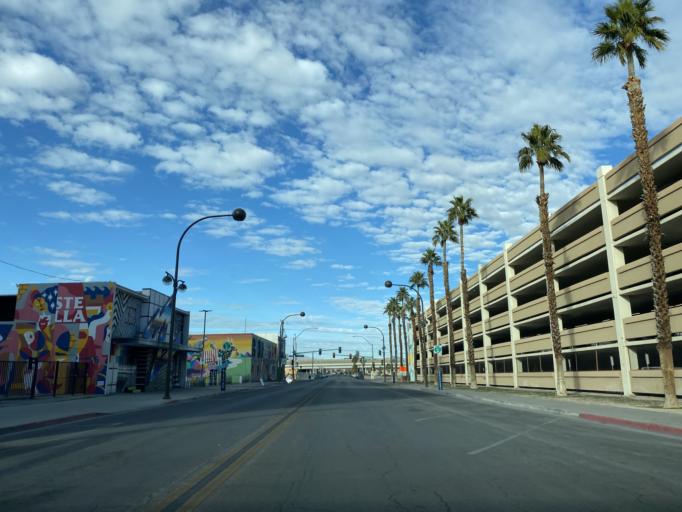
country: US
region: Nevada
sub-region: Clark County
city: Las Vegas
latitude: 36.1695
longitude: -115.1376
